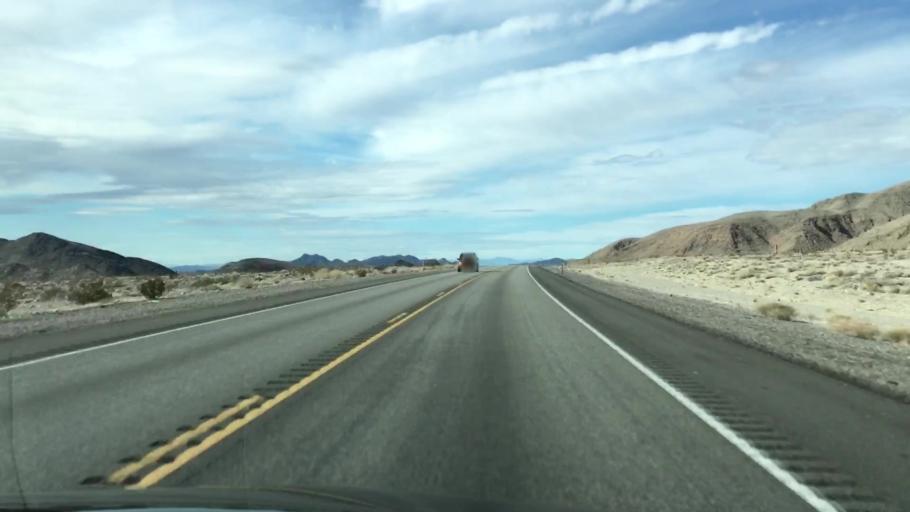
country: US
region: Nevada
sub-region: Nye County
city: Pahrump
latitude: 36.5756
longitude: -116.1899
